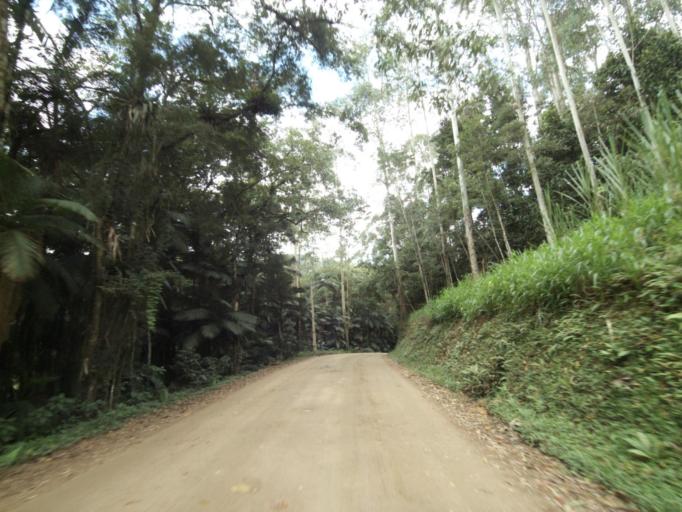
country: BR
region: Santa Catarina
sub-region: Pomerode
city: Pomerode
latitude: -26.7034
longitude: -49.2159
